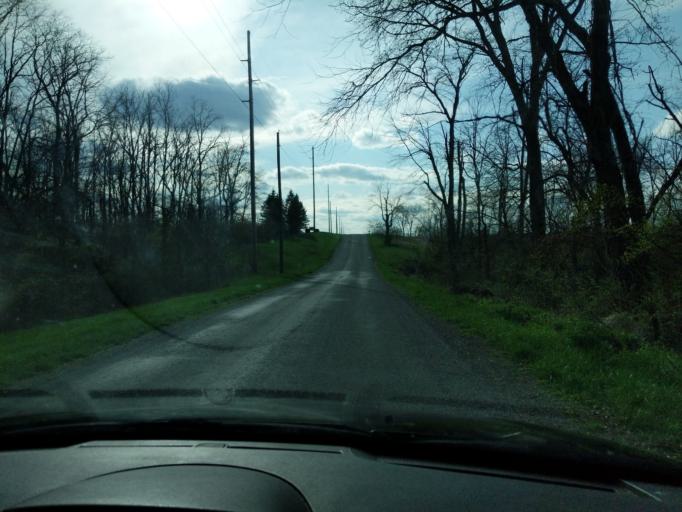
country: US
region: Ohio
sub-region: Champaign County
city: North Lewisburg
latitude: 40.1635
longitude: -83.6517
